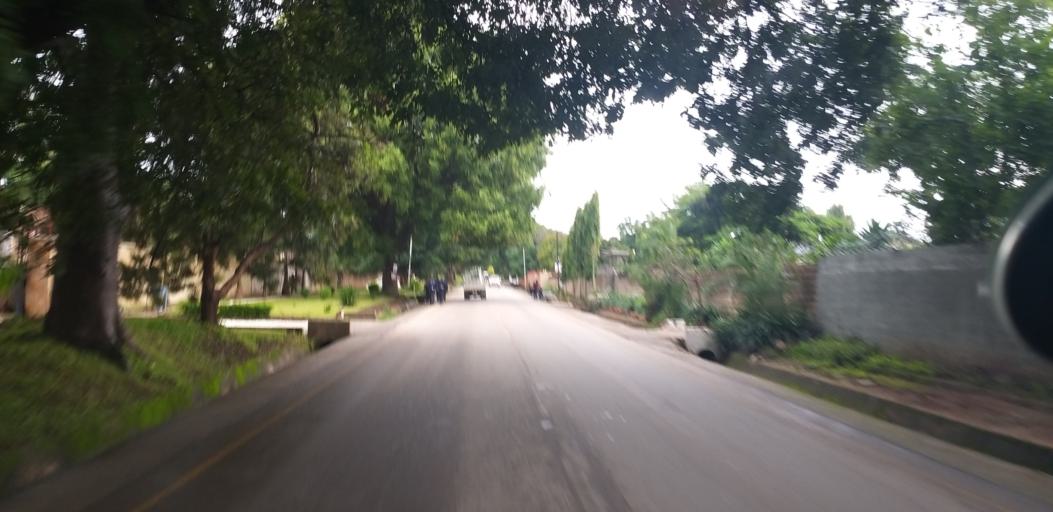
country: ZM
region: Lusaka
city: Lusaka
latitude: -15.4204
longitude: 28.2966
